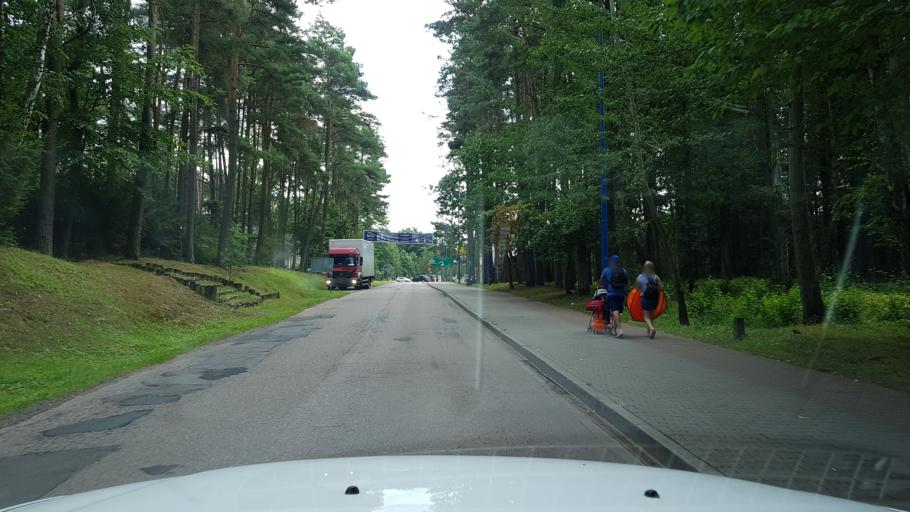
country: PL
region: West Pomeranian Voivodeship
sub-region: Powiat gryficki
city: Pobierowo
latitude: 54.0568
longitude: 14.9401
